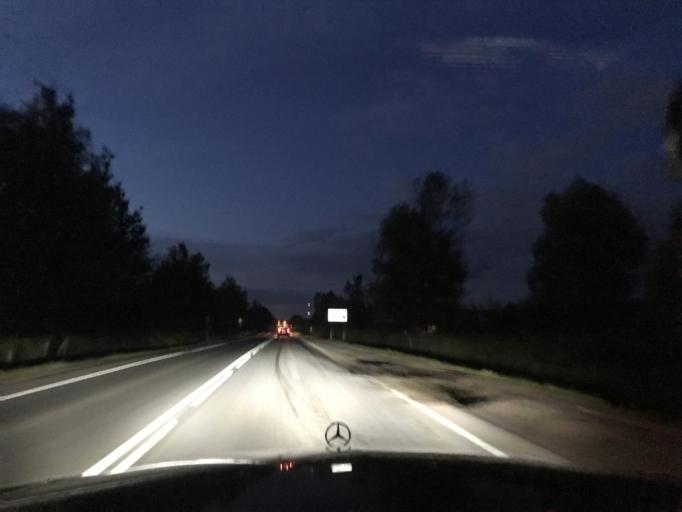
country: BY
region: Brest
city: Brest
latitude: 52.0414
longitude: 23.7282
